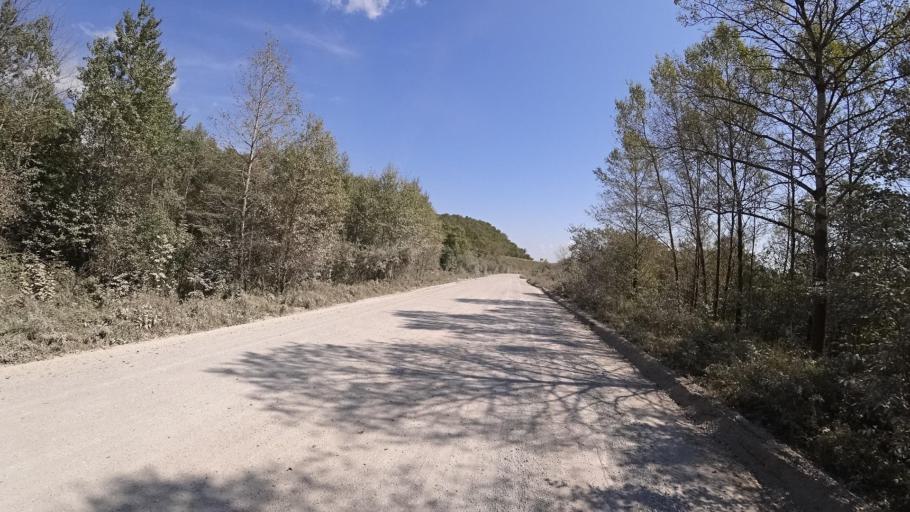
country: RU
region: Jewish Autonomous Oblast
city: Londoko
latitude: 49.0044
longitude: 131.9178
